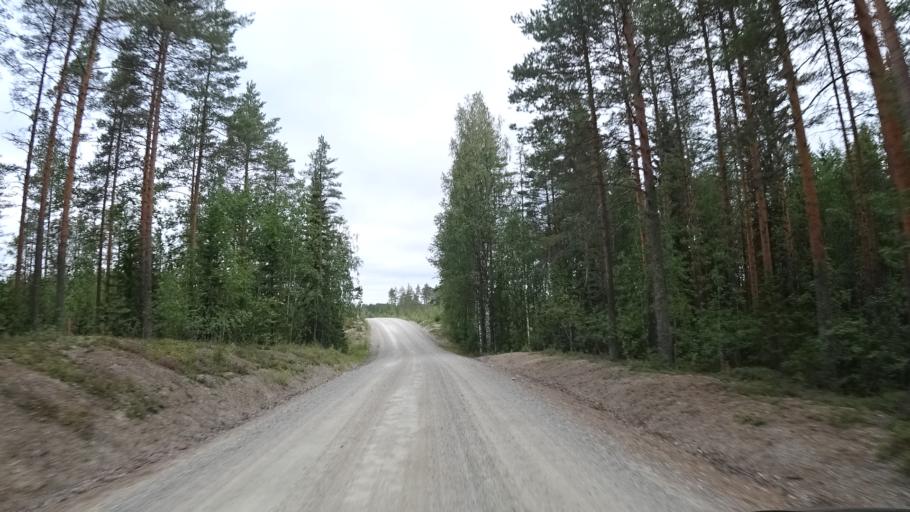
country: FI
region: North Karelia
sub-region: Pielisen Karjala
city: Lieksa
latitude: 63.2496
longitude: 30.3337
